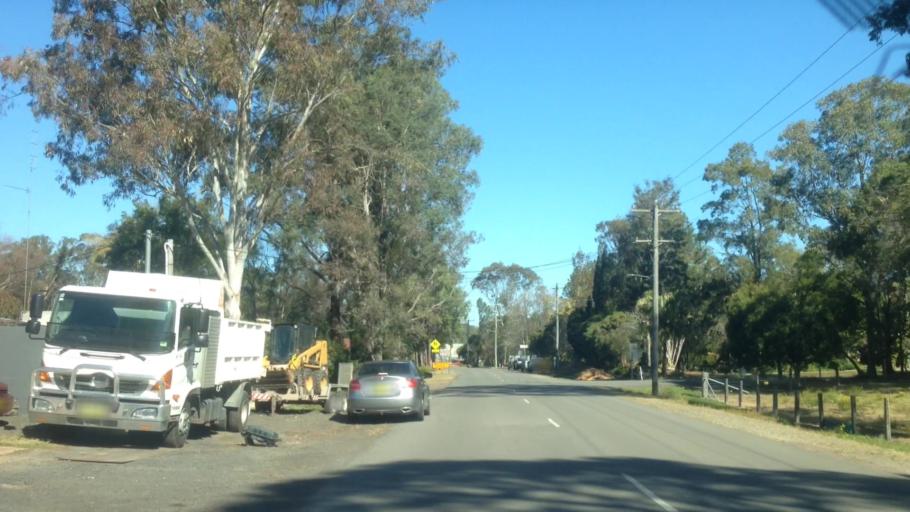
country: AU
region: New South Wales
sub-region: Lake Macquarie Shire
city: Cooranbong
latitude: -33.0883
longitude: 151.4496
